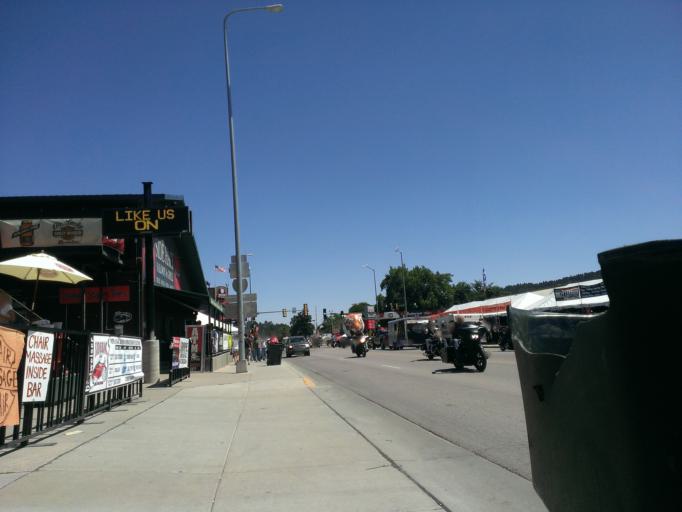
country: US
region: South Dakota
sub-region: Meade County
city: Sturgis
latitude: 44.4156
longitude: -103.5103
